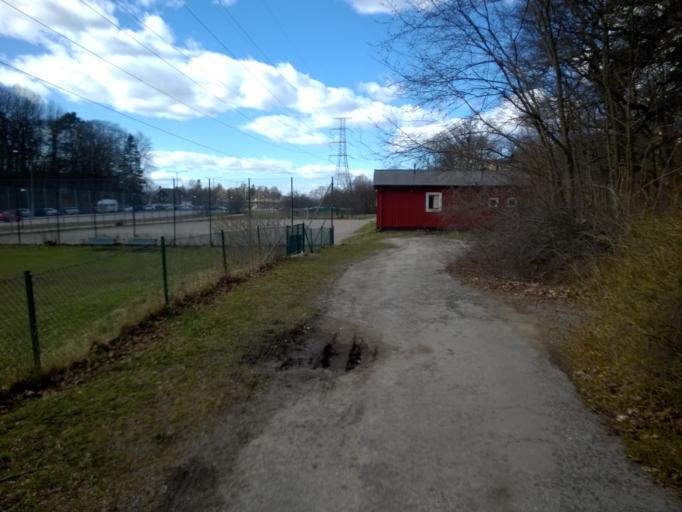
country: SE
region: Stockholm
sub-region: Norrtalje Kommun
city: Bergshamra
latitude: 59.3703
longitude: 18.0572
